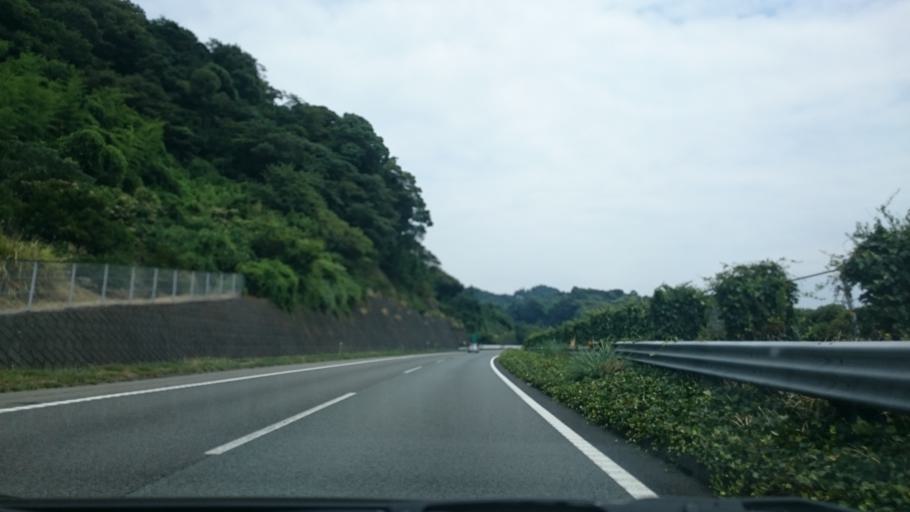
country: JP
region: Shizuoka
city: Fujinomiya
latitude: 35.1140
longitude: 138.5772
